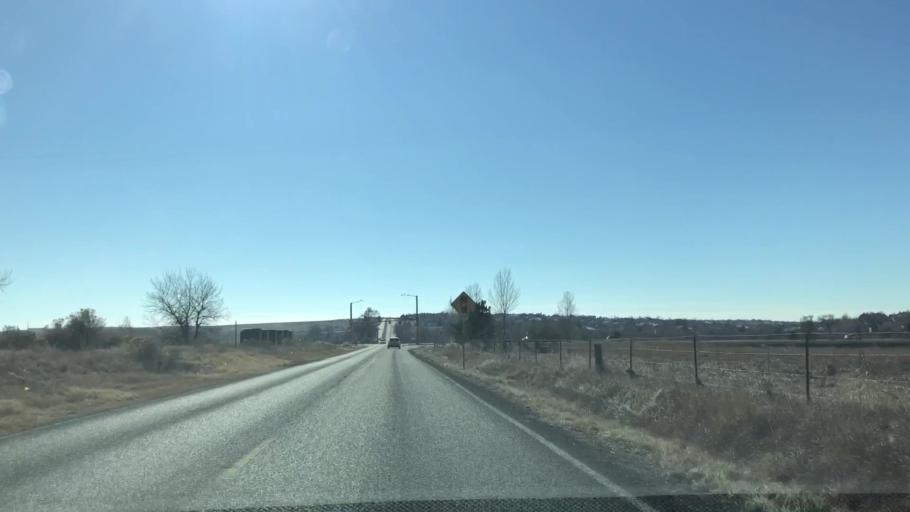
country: US
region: Colorado
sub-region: Weld County
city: Windsor
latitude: 40.4812
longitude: -104.9442
